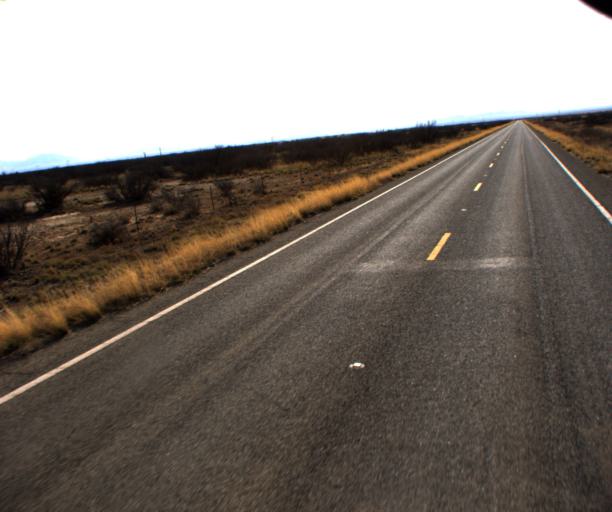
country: US
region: Arizona
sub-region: Cochise County
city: Willcox
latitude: 32.1953
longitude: -109.7436
